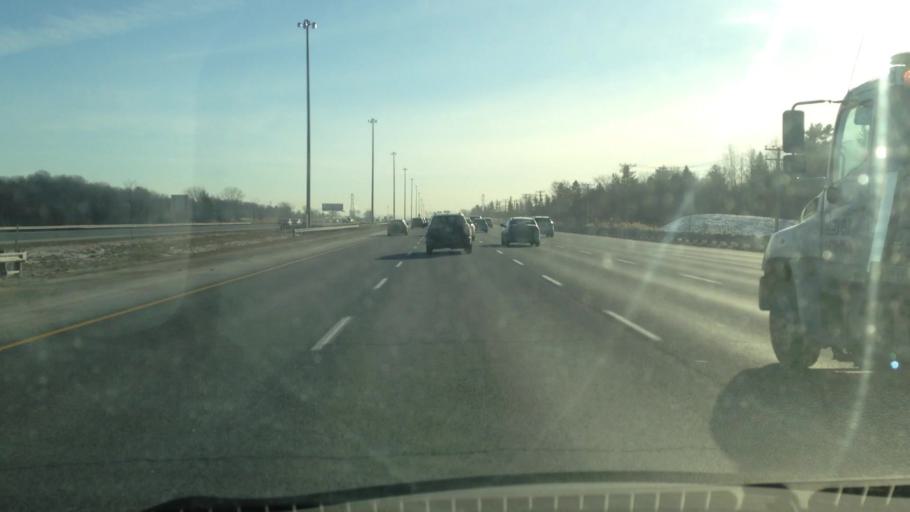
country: CA
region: Quebec
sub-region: Laurentides
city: Blainville
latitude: 45.6534
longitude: -73.8787
